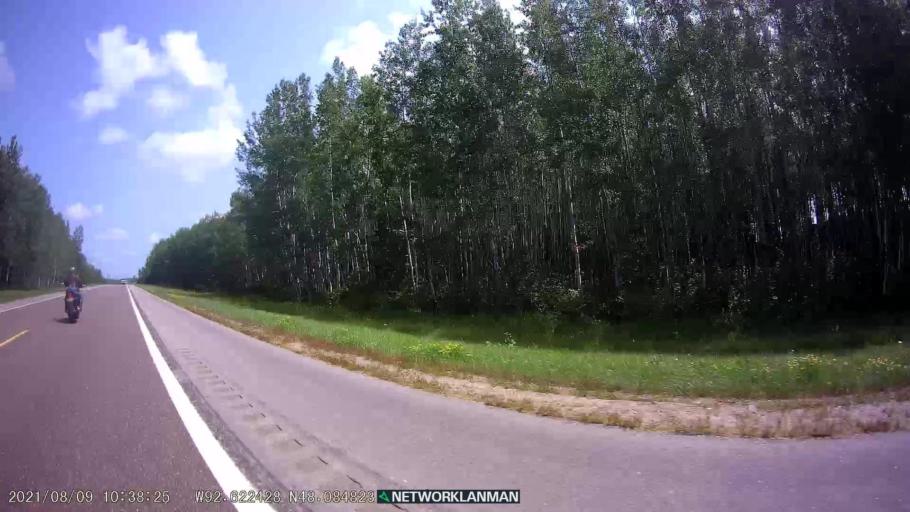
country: US
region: Minnesota
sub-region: Saint Louis County
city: Mountain Iron
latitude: 48.0852
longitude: -92.6221
